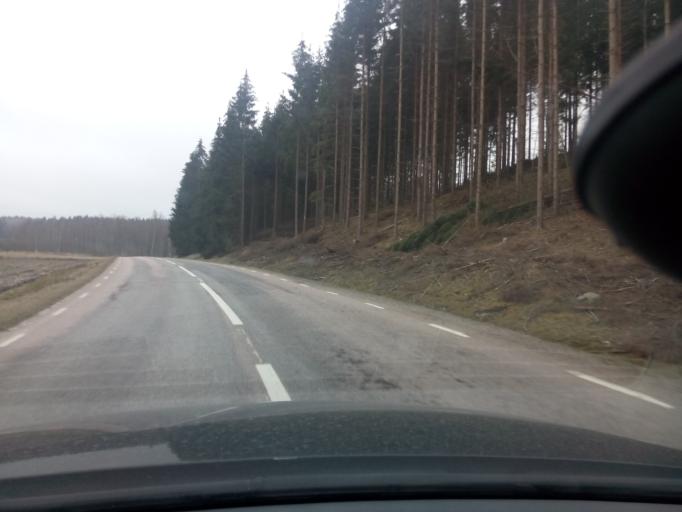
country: SE
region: Soedermanland
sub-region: Gnesta Kommun
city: Gnesta
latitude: 59.0451
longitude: 17.1582
